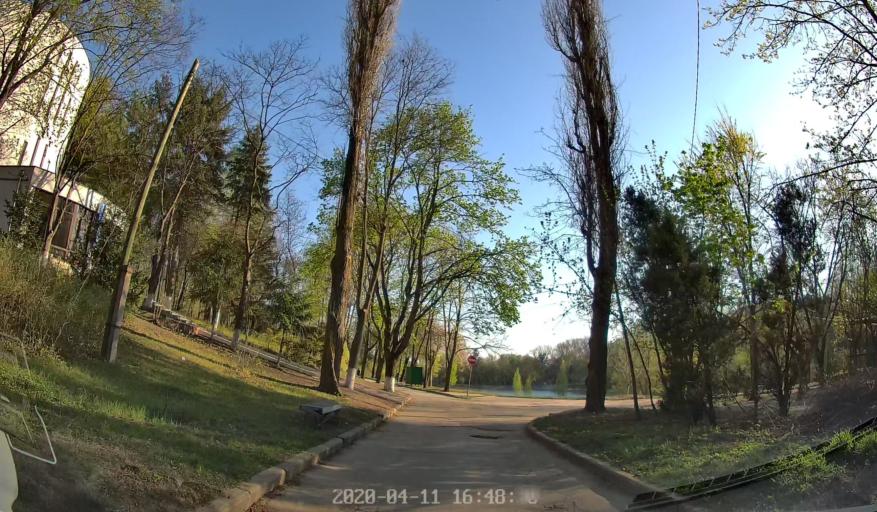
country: MD
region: Chisinau
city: Chisinau
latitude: 47.0405
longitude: 28.8718
